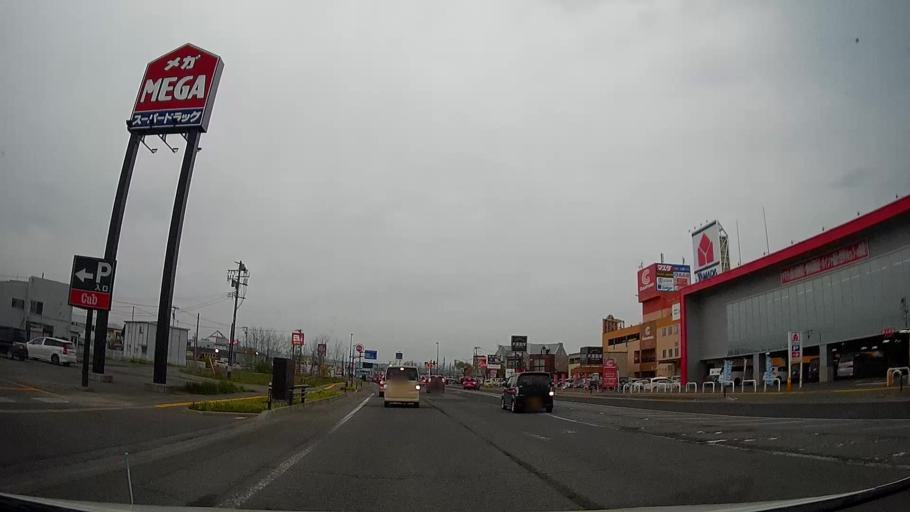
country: JP
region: Aomori
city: Aomori Shi
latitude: 40.8315
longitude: 140.7029
